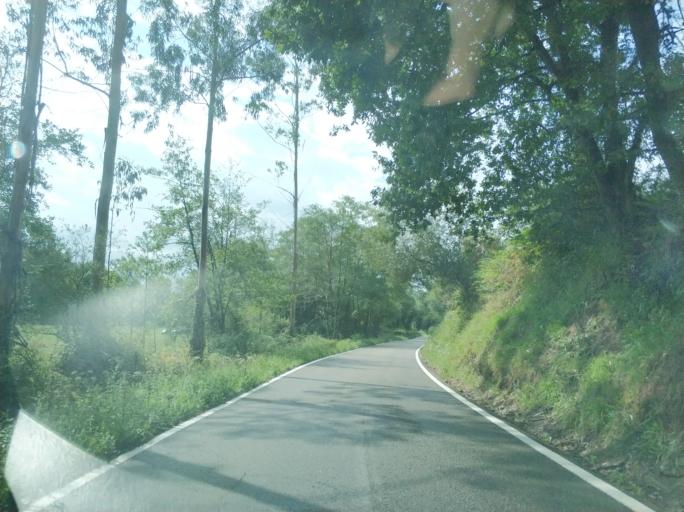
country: ES
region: Cantabria
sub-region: Provincia de Cantabria
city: Polanco
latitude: 43.3799
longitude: -3.9721
